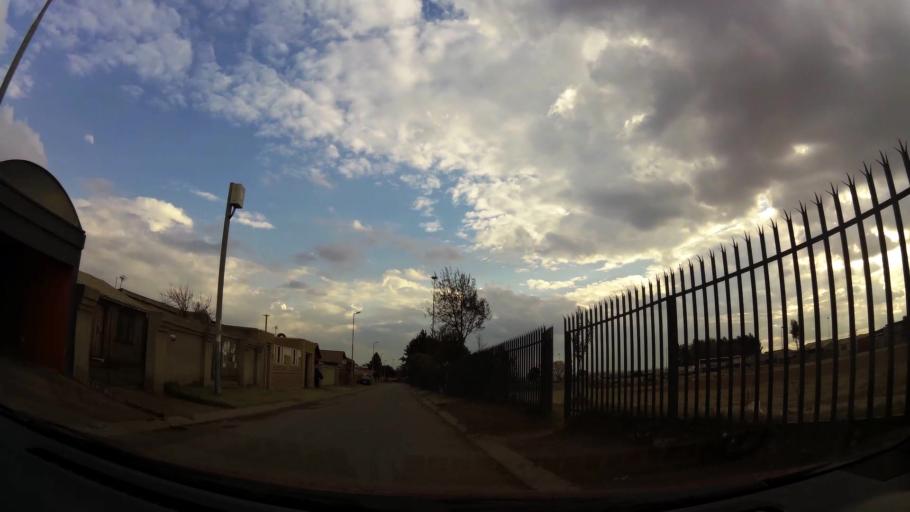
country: ZA
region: Gauteng
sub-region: City of Johannesburg Metropolitan Municipality
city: Soweto
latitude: -26.2401
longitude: 27.8272
